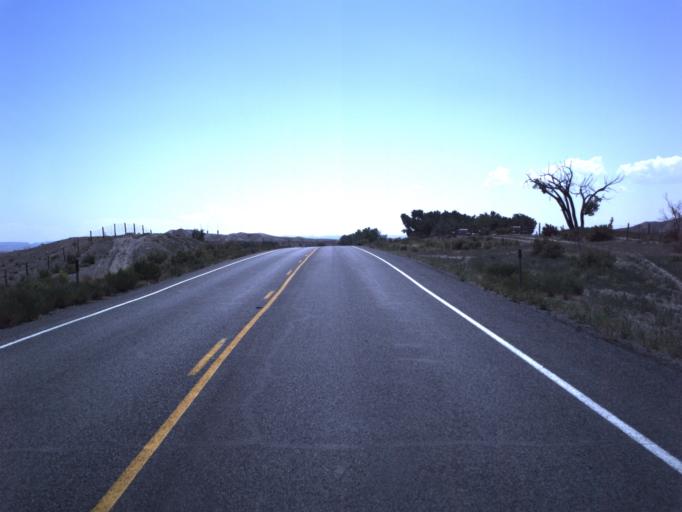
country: US
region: Utah
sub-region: Emery County
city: Orangeville
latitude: 39.2274
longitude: -111.0729
